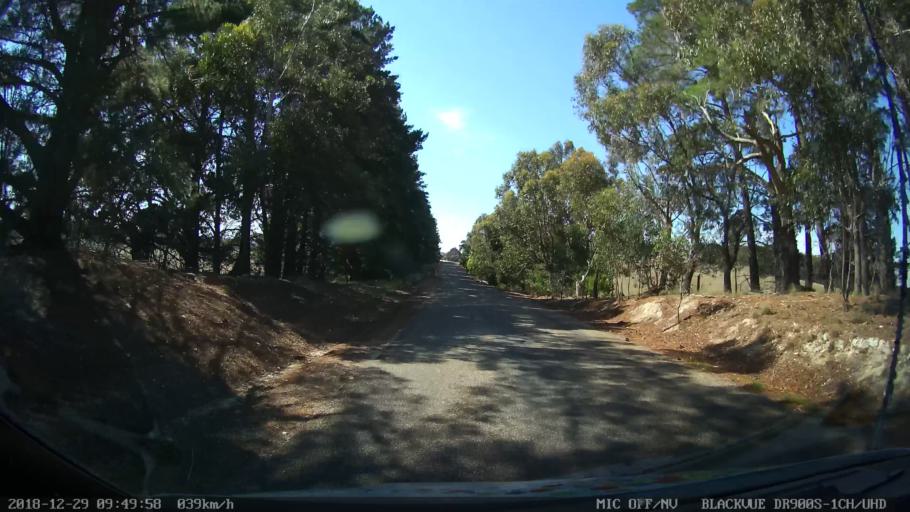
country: AU
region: New South Wales
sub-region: Upper Lachlan Shire
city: Crookwell
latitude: -34.7180
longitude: 149.4566
